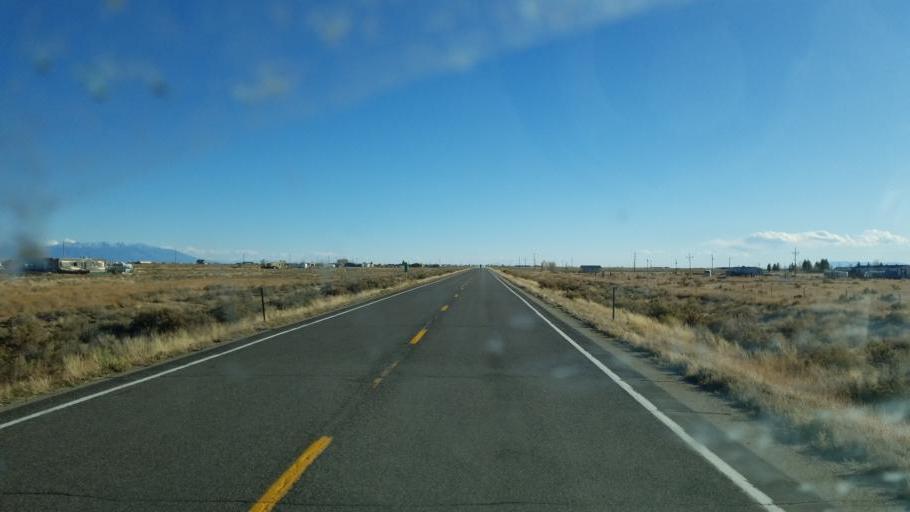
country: US
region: Colorado
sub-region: Saguache County
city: Saguache
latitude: 38.1368
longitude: -105.9237
